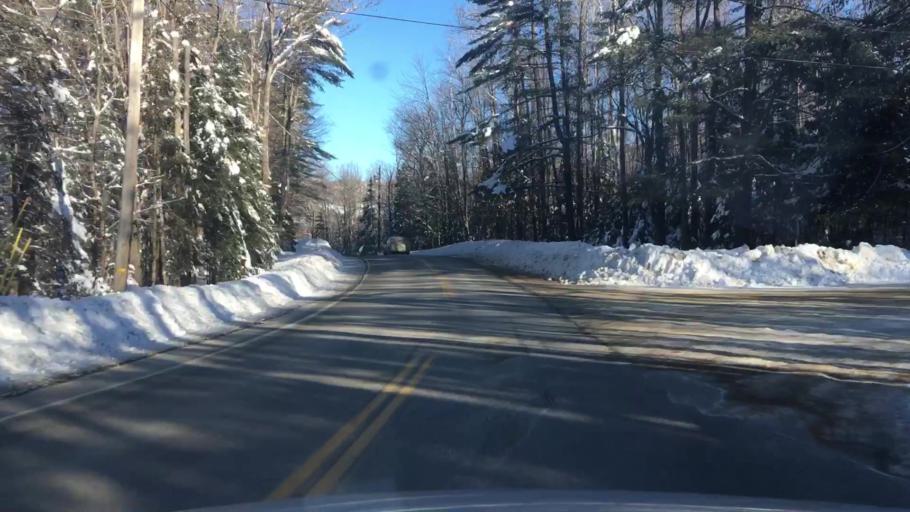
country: US
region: Maine
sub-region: Oxford County
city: West Paris
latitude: 44.4002
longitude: -70.6340
